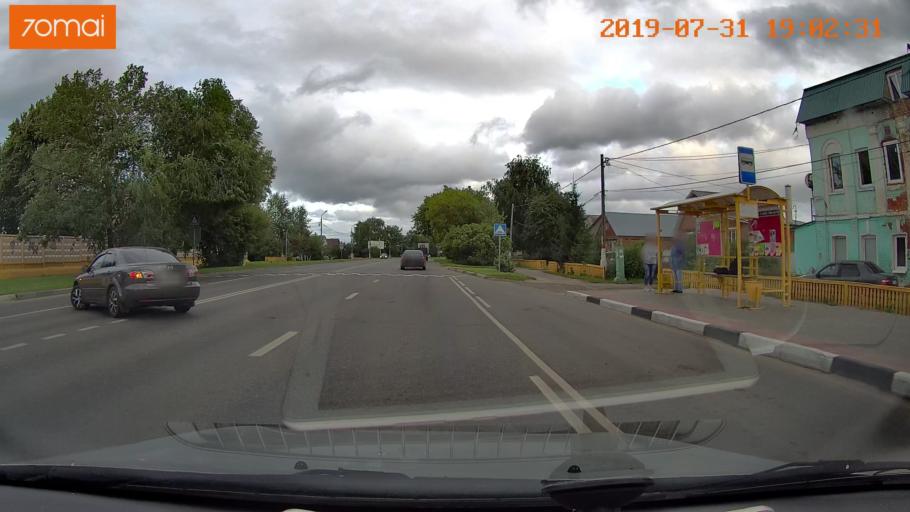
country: RU
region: Moskovskaya
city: Raduzhnyy
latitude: 55.1197
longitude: 38.7330
